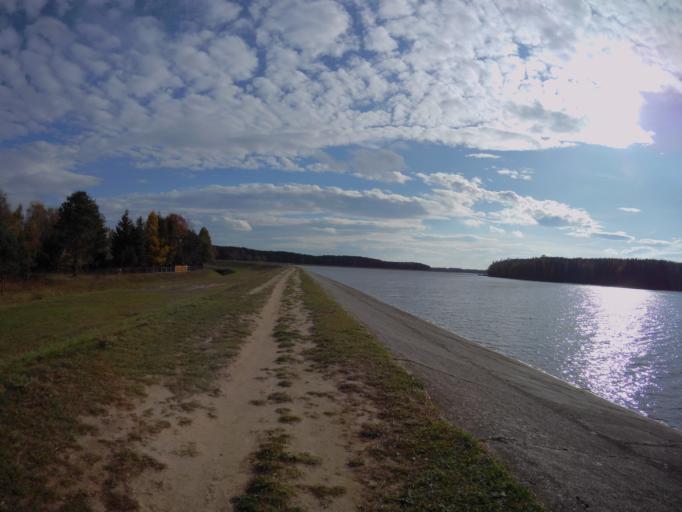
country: PL
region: Subcarpathian Voivodeship
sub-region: Powiat kolbuszowski
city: Lipnica
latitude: 50.3399
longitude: 21.9363
